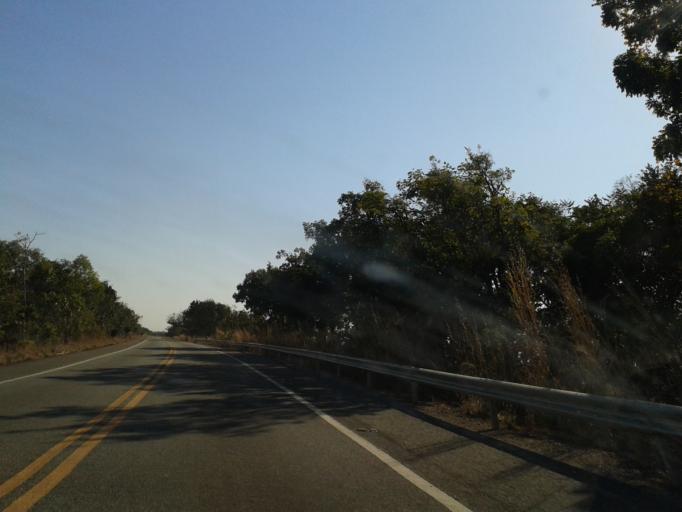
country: BR
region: Goias
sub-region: Mozarlandia
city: Mozarlandia
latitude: -14.9256
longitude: -50.5540
